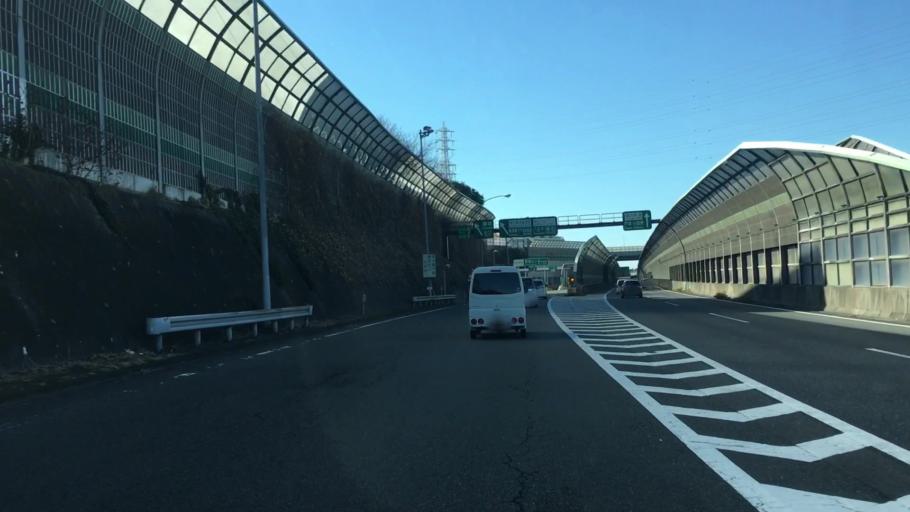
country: JP
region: Kanagawa
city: Yokohama
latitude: 35.4530
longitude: 139.5782
